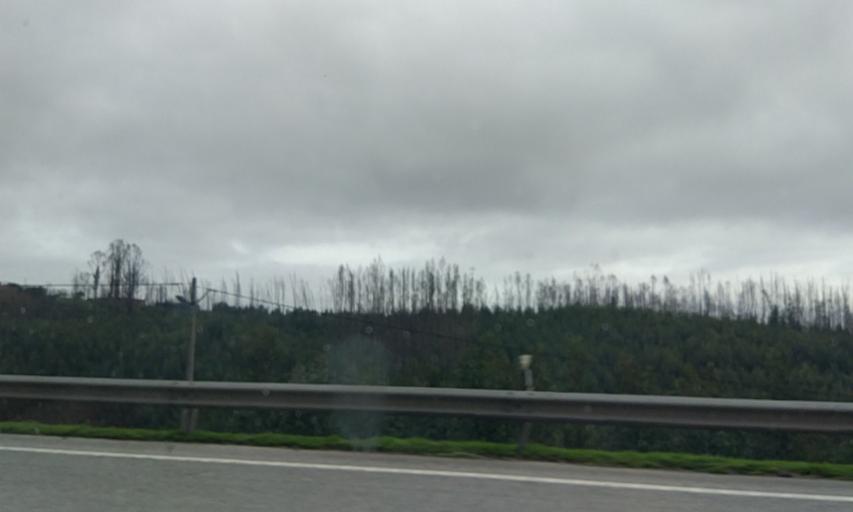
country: PT
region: Viseu
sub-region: Santa Comba Dao
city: Santa Comba Dao
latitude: 40.3570
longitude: -8.1448
